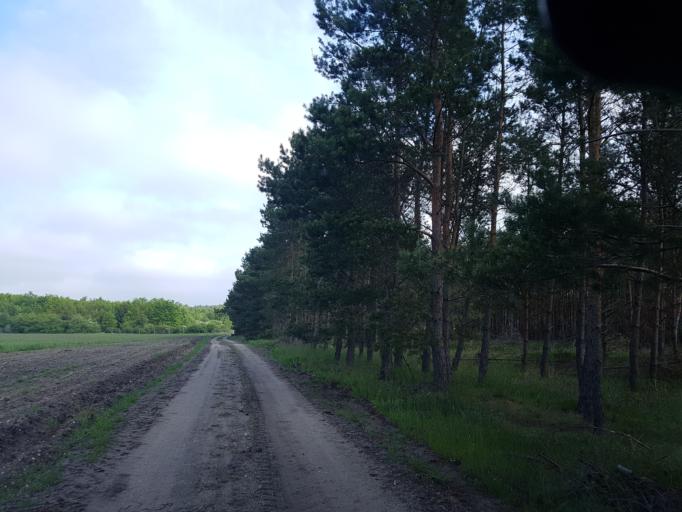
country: DE
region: Brandenburg
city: Finsterwalde
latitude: 51.5747
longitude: 13.6578
